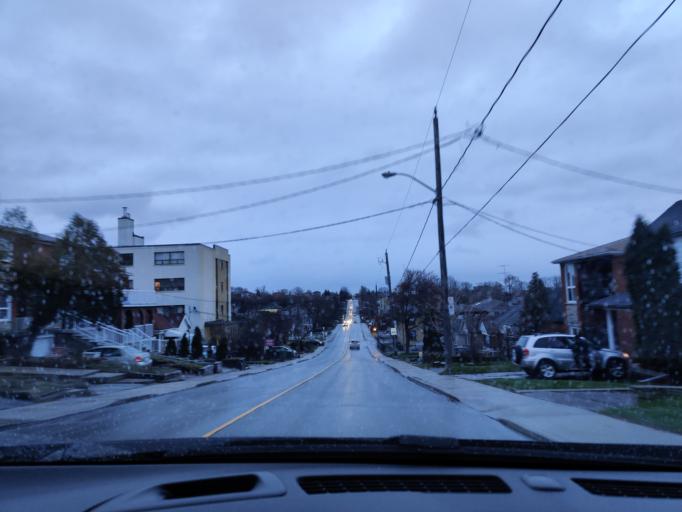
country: CA
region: Ontario
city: Toronto
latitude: 43.6917
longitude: -79.4617
